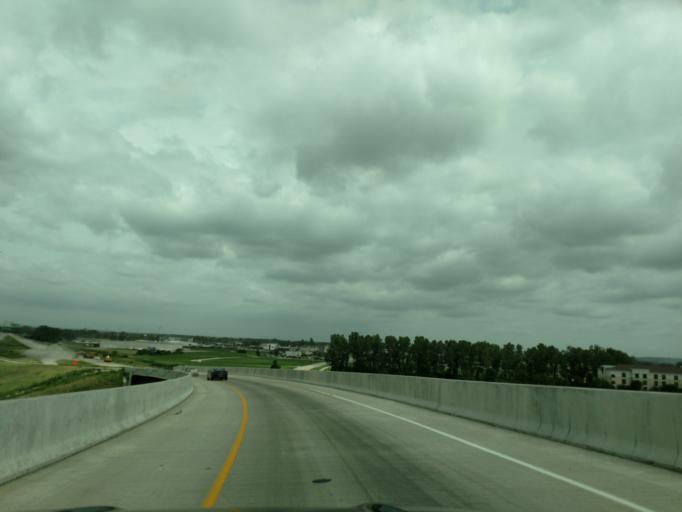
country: US
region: Iowa
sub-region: Pottawattamie County
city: Council Bluffs
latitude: 41.2338
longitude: -95.8958
